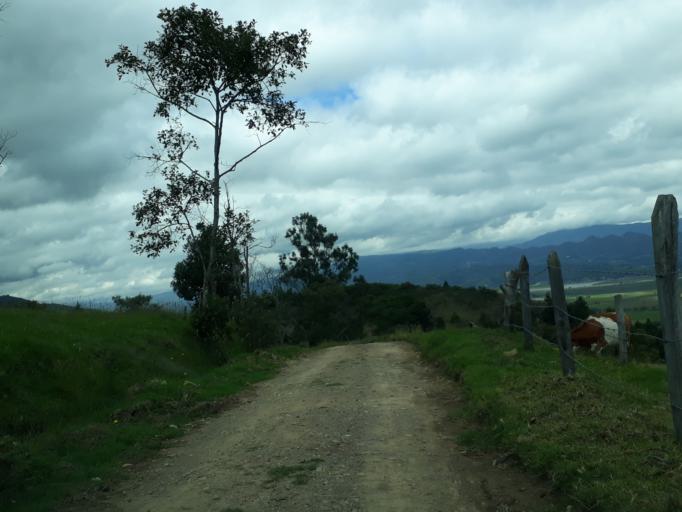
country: CO
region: Cundinamarca
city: Guacheta
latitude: 5.4385
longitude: -73.7026
